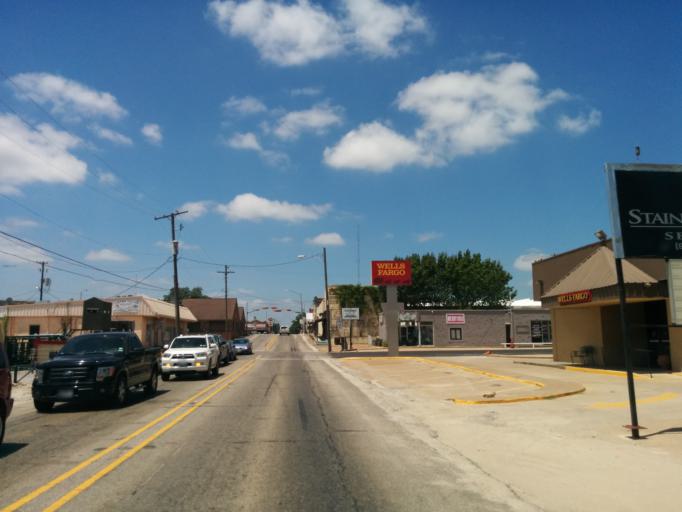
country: US
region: Texas
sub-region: Madison County
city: Madisonville
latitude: 30.9497
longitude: -95.9125
